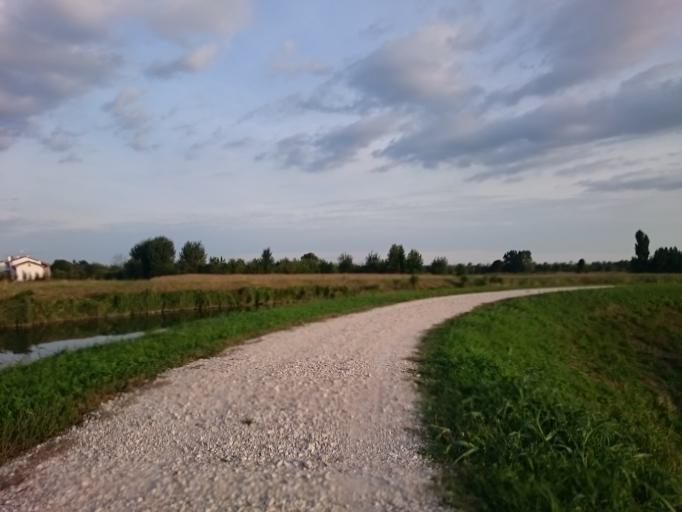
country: IT
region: Veneto
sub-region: Provincia di Padova
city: Campodoro
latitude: 45.5032
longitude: 11.7334
